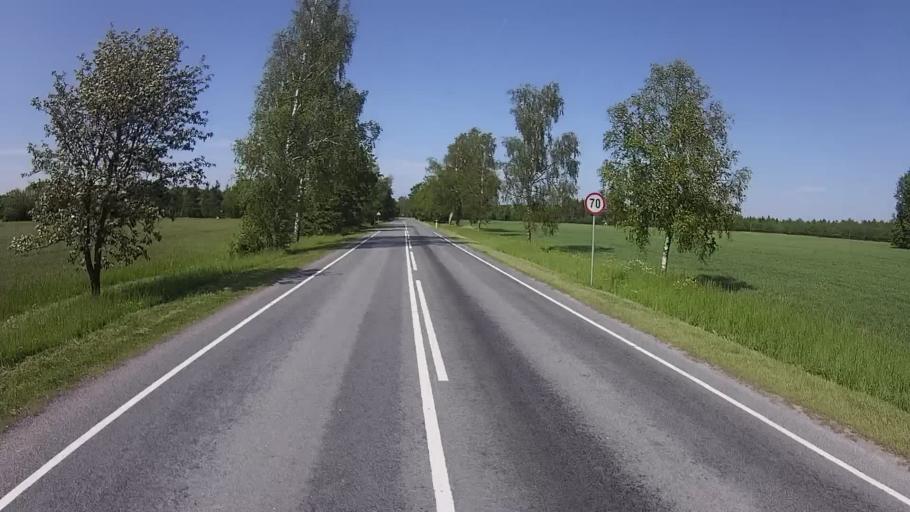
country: EE
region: Saare
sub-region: Kuressaare linn
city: Kuressaare
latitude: 58.3368
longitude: 22.4520
